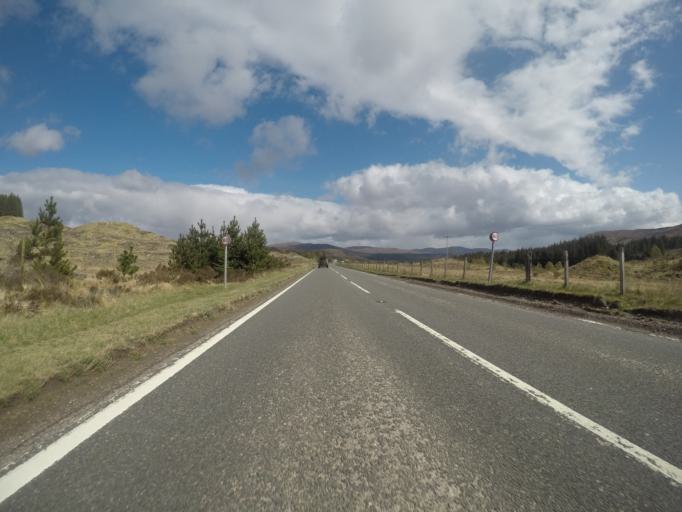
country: GB
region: Scotland
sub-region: Highland
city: Spean Bridge
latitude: 57.1381
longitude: -4.9539
